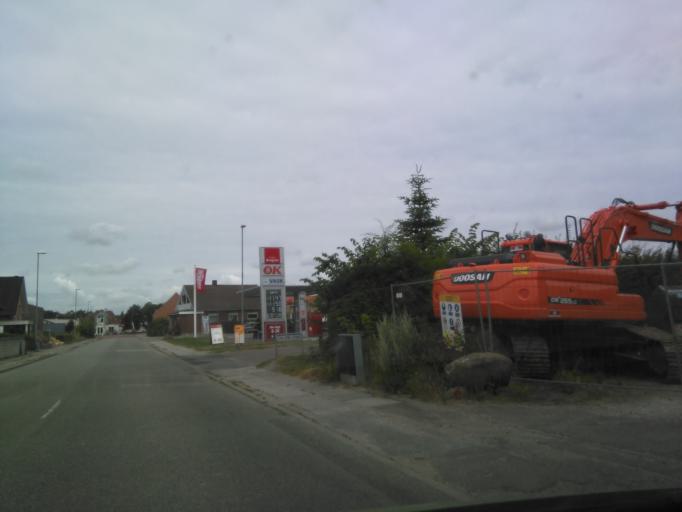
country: DK
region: Central Jutland
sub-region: Arhus Kommune
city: Solbjerg
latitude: 56.0370
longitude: 10.0839
